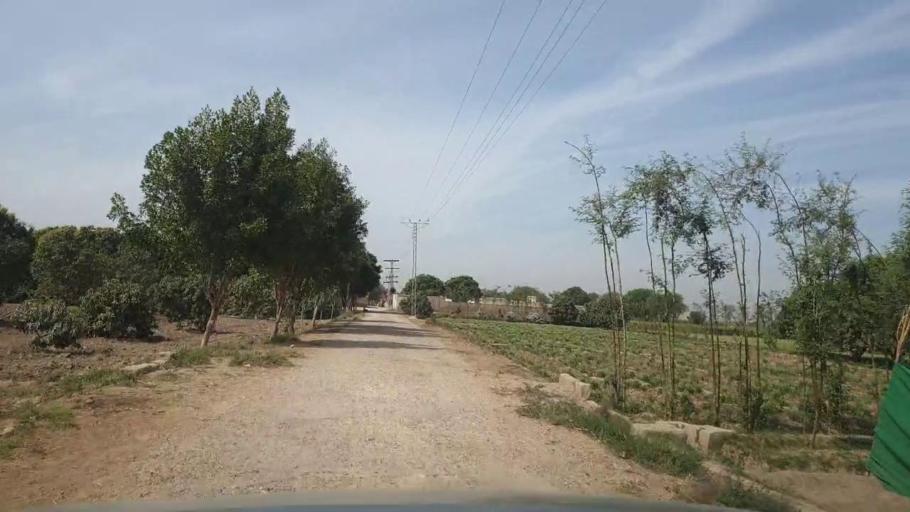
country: PK
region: Sindh
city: Kunri
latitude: 25.1278
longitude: 69.5929
